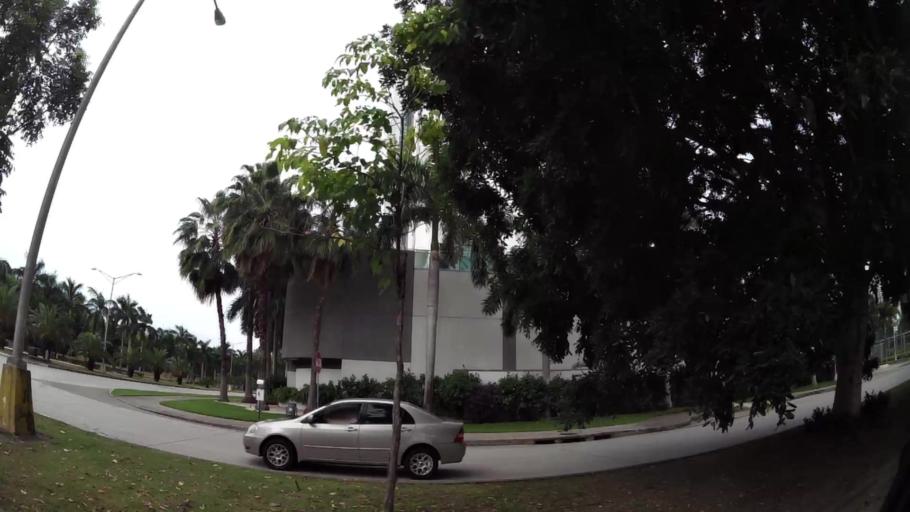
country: PA
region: Panama
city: San Miguelito
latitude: 9.0108
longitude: -79.4613
